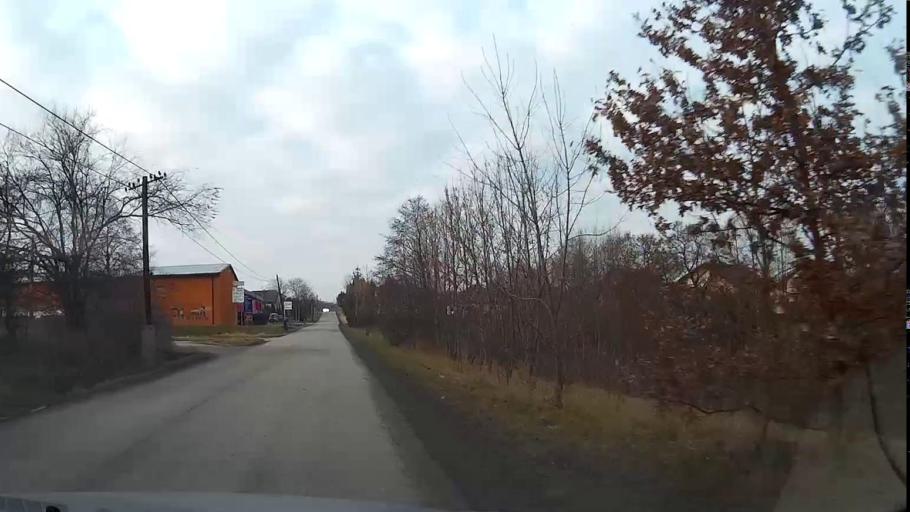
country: PL
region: Lesser Poland Voivodeship
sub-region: Powiat chrzanowski
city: Alwernia
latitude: 50.0631
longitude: 19.5488
